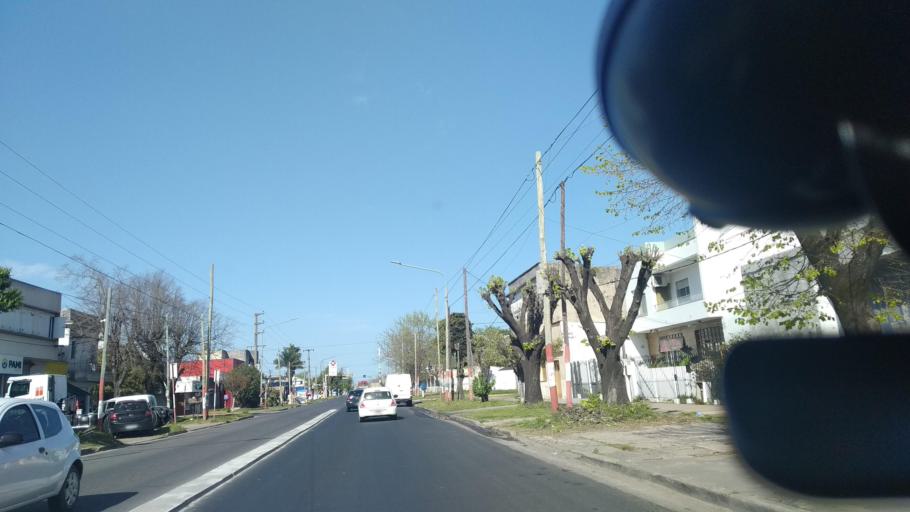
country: AR
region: Buenos Aires
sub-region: Partido de La Plata
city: La Plata
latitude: -34.9587
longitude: -57.9707
